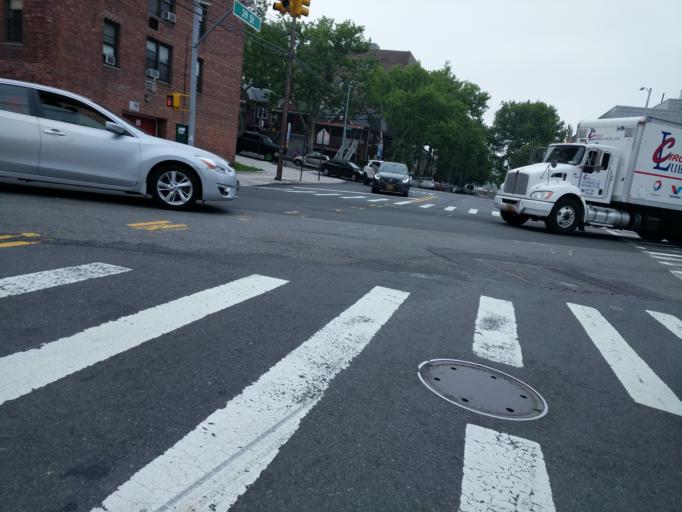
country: US
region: New York
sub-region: Queens County
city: Long Island City
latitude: 40.7388
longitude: -73.9272
